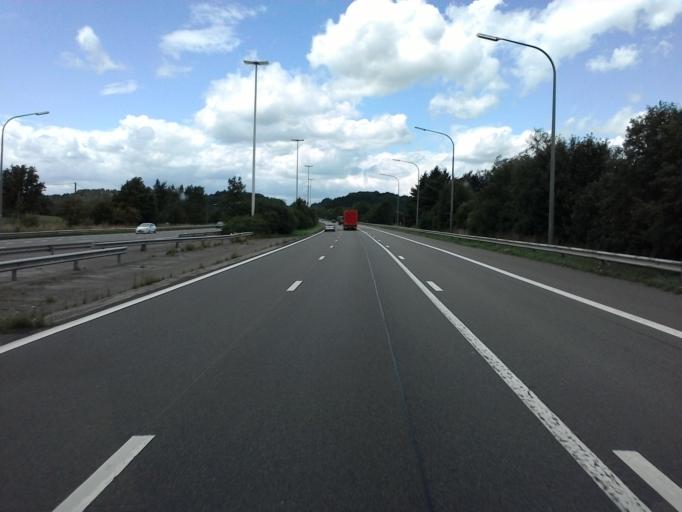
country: BE
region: Wallonia
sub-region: Province de Liege
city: Aywaille
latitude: 50.4951
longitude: 5.7082
